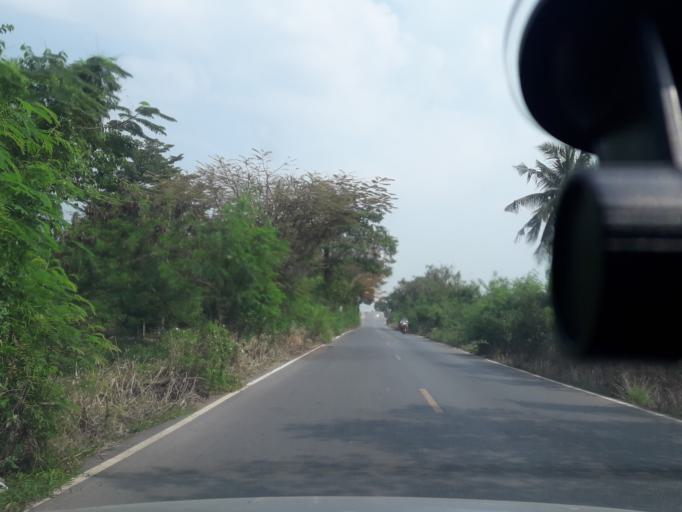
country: TH
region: Pathum Thani
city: Nong Suea
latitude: 14.1967
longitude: 100.8896
